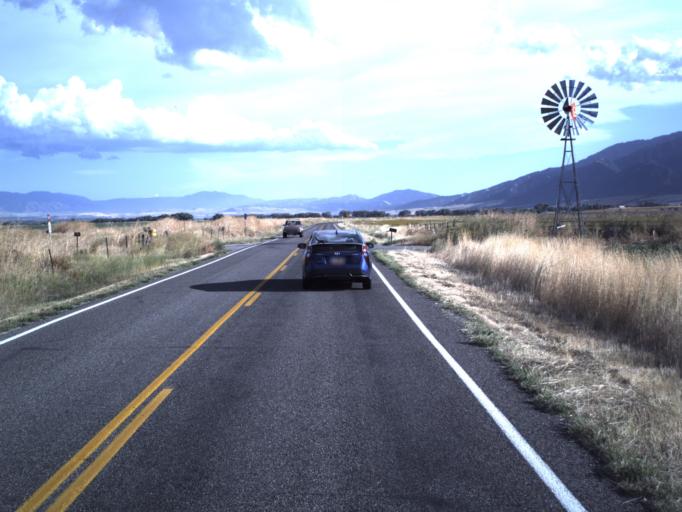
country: US
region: Utah
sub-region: Cache County
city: Benson
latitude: 41.7652
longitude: -111.9805
